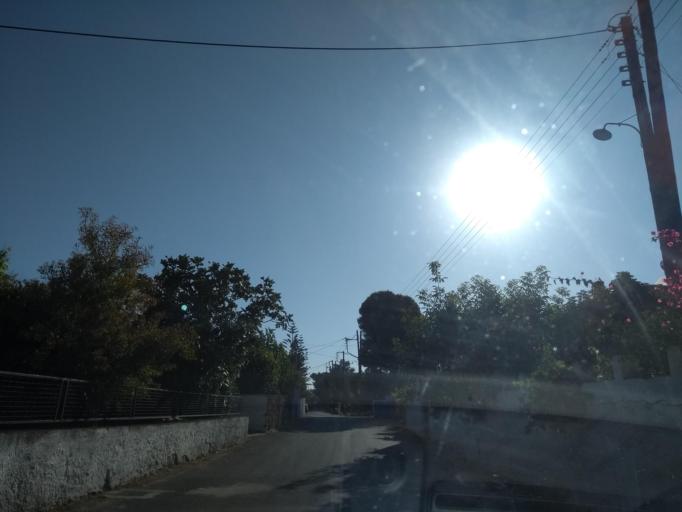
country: GR
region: Crete
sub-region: Nomos Chanias
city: Pithari
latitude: 35.5184
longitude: 24.0763
